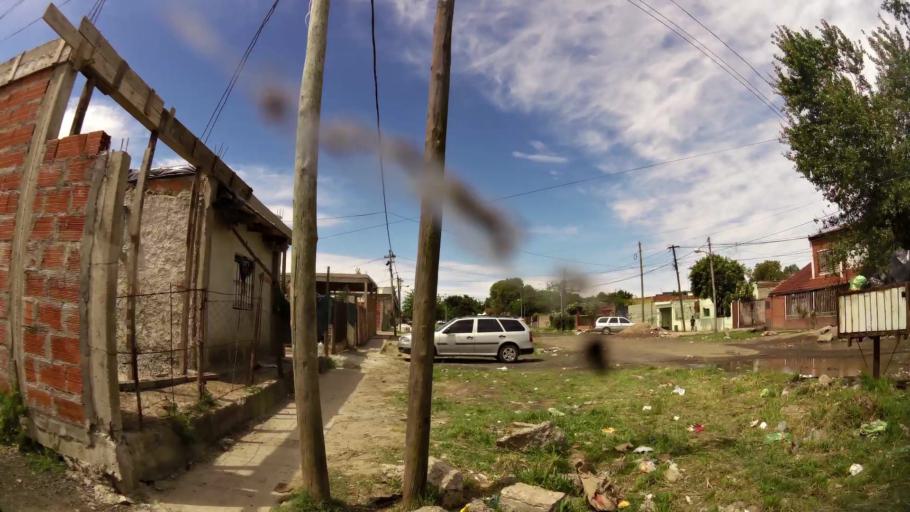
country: AR
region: Buenos Aires
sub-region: Partido de Quilmes
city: Quilmes
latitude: -34.7589
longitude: -58.3021
